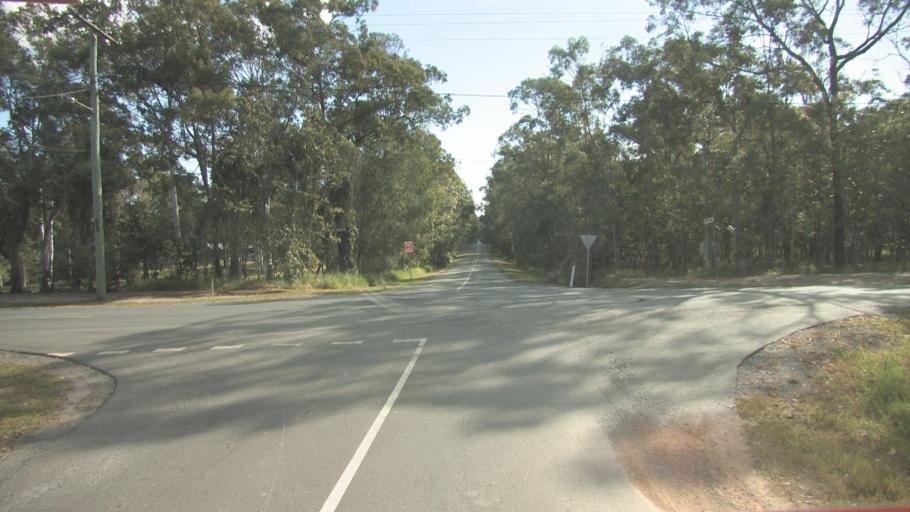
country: AU
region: Queensland
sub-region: Gold Coast
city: Yatala
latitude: -27.6684
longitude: 153.2447
